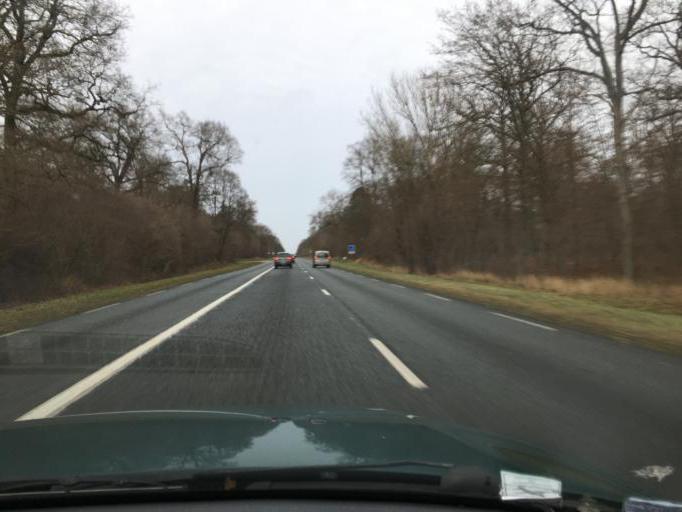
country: FR
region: Picardie
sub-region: Departement de l'Oise
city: Thiers-sur-Theve
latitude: 49.1672
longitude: 2.5574
